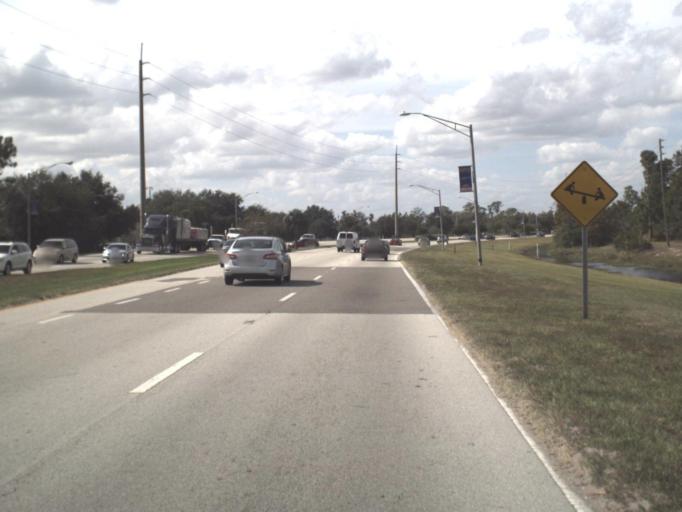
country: US
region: Florida
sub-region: Osceola County
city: Poinciana
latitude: 28.1459
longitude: -81.4557
